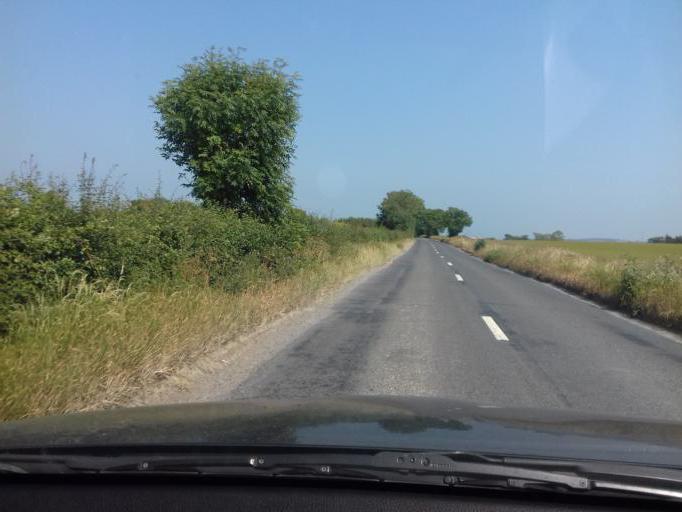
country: IE
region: Leinster
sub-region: An Mhi
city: Stamullin
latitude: 53.5975
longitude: -6.2379
